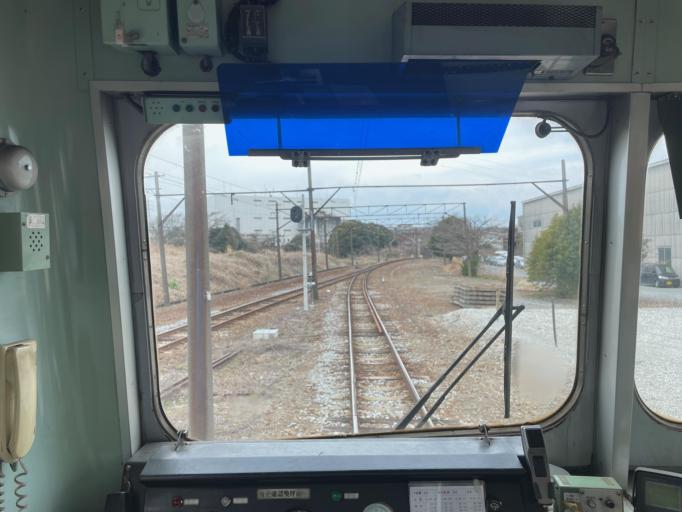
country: JP
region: Shizuoka
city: Fuji
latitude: 35.1617
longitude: 138.7130
